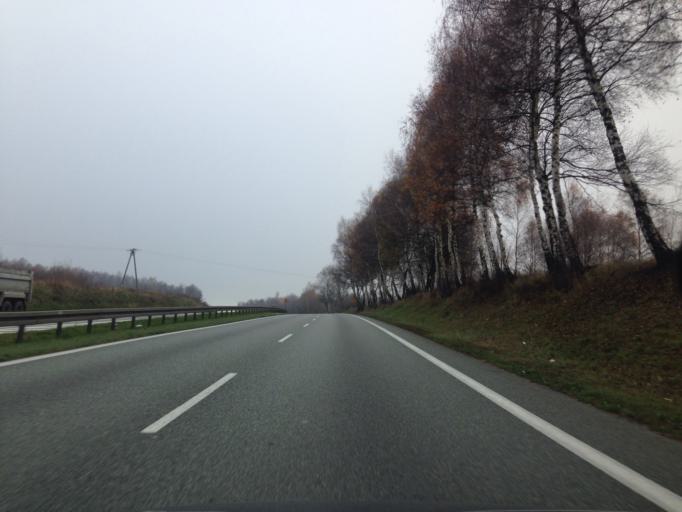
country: PL
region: Silesian Voivodeship
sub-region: Powiat bedzinski
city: Siewierz
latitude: 50.4391
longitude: 19.2173
